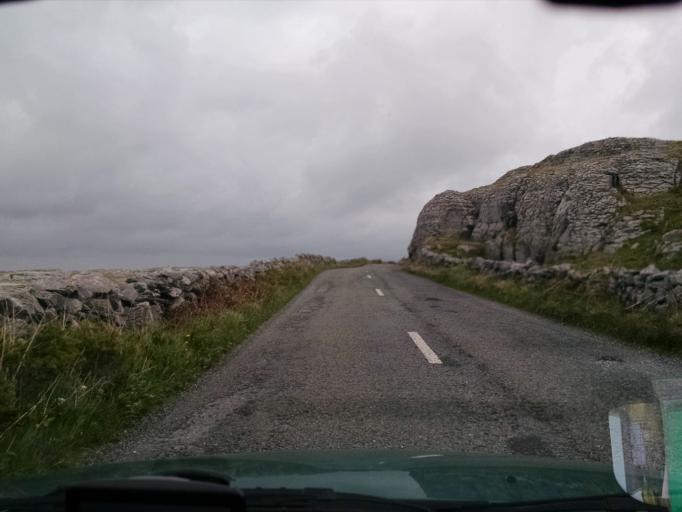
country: IE
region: Connaught
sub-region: County Galway
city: Bearna
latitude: 53.0722
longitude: -9.3554
